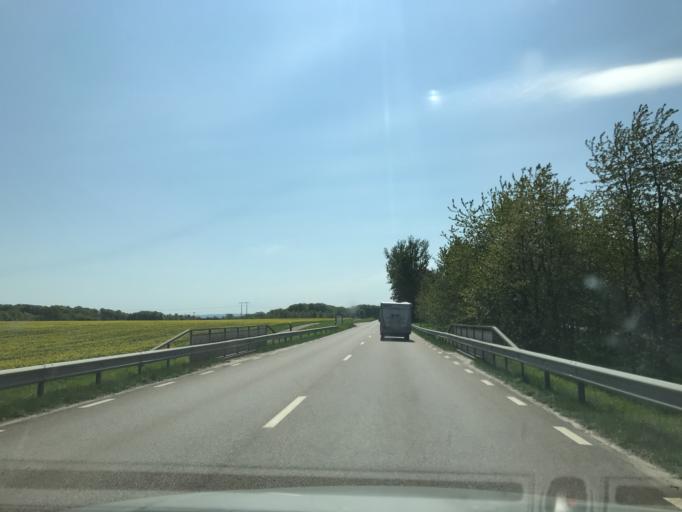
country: SE
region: Skane
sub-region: Angelholms Kommun
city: Munka-Ljungby
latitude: 56.2285
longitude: 13.0365
